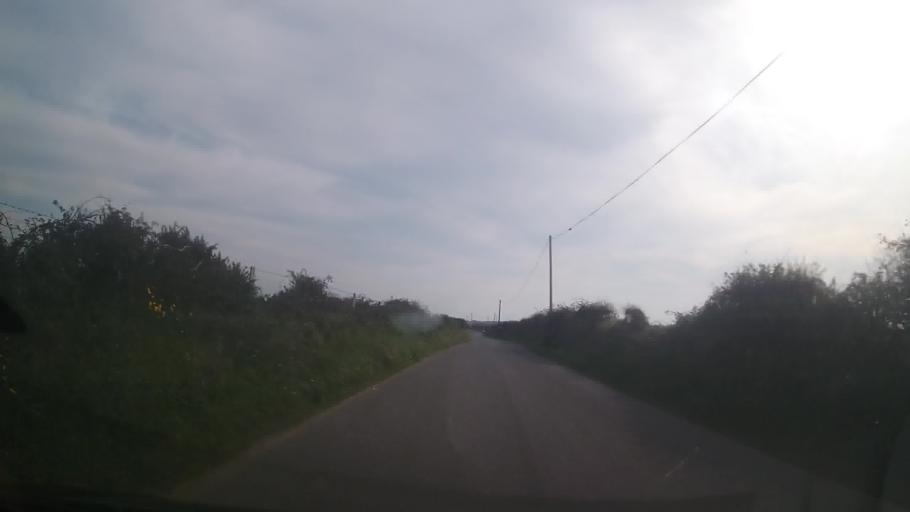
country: GB
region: Wales
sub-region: Pembrokeshire
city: Saint David's
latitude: 51.9117
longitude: -5.2408
